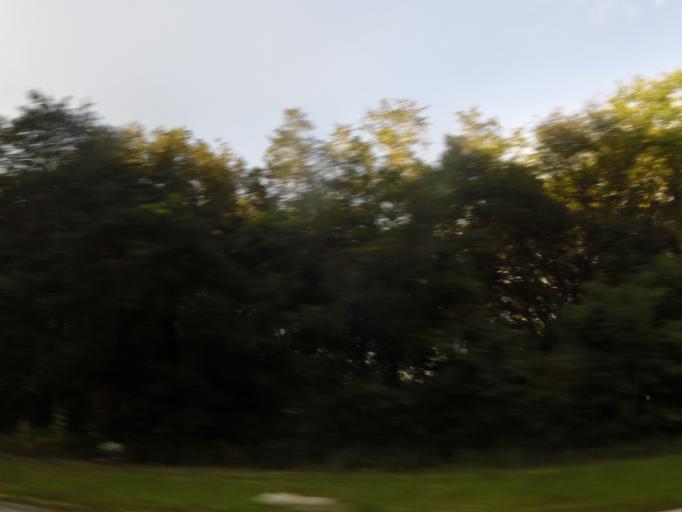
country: US
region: Florida
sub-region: Duval County
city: Atlantic Beach
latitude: 30.3780
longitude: -81.4897
